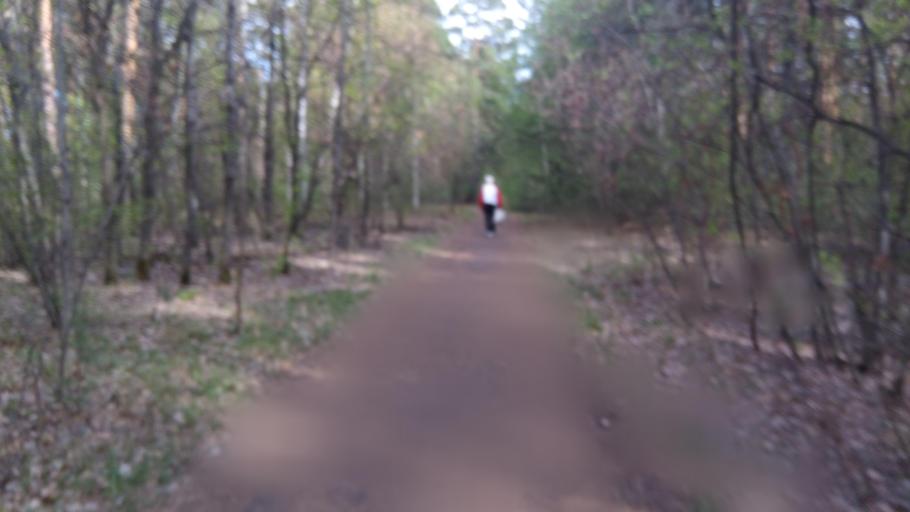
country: RU
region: Chelyabinsk
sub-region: Gorod Chelyabinsk
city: Chelyabinsk
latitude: 55.1613
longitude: 61.3497
